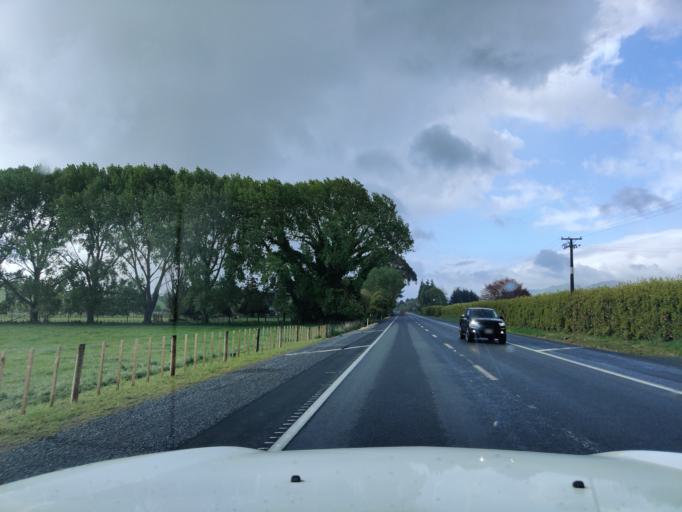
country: NZ
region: Waikato
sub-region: Waipa District
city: Cambridge
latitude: -37.9339
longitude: 175.5737
